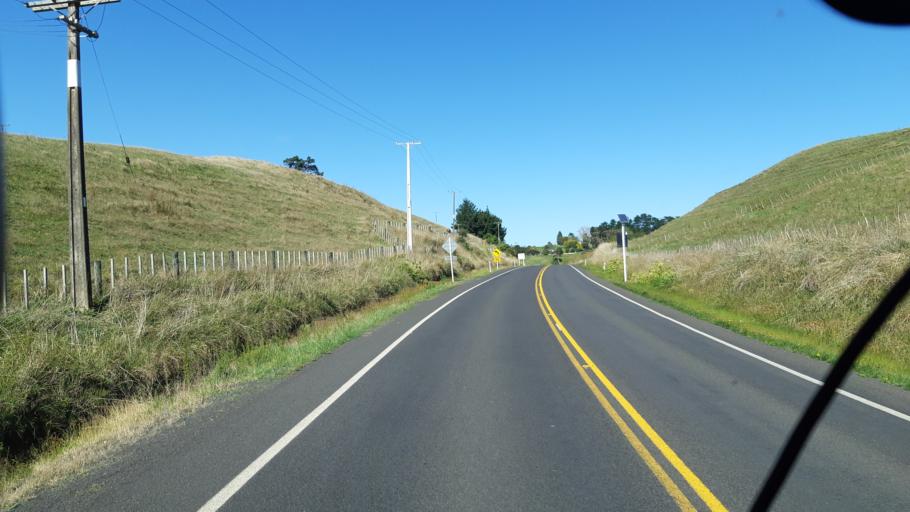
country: NZ
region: Manawatu-Wanganui
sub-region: Wanganui District
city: Wanganui
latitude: -39.9626
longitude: 175.1002
